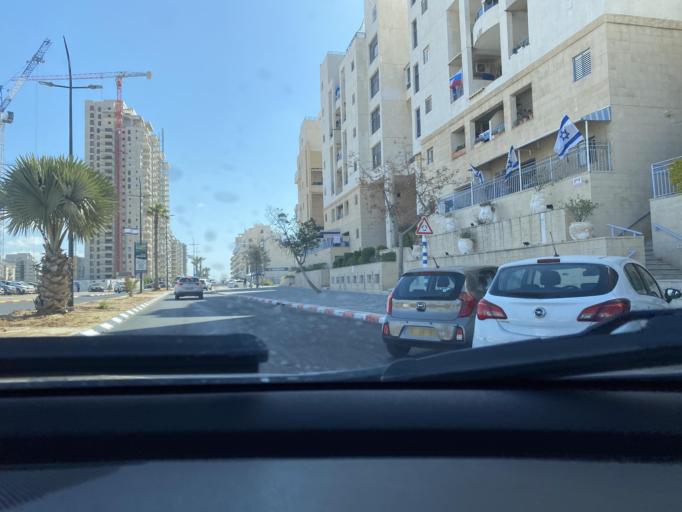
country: IL
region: Southern District
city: Ashqelon
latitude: 31.6819
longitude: 34.5594
